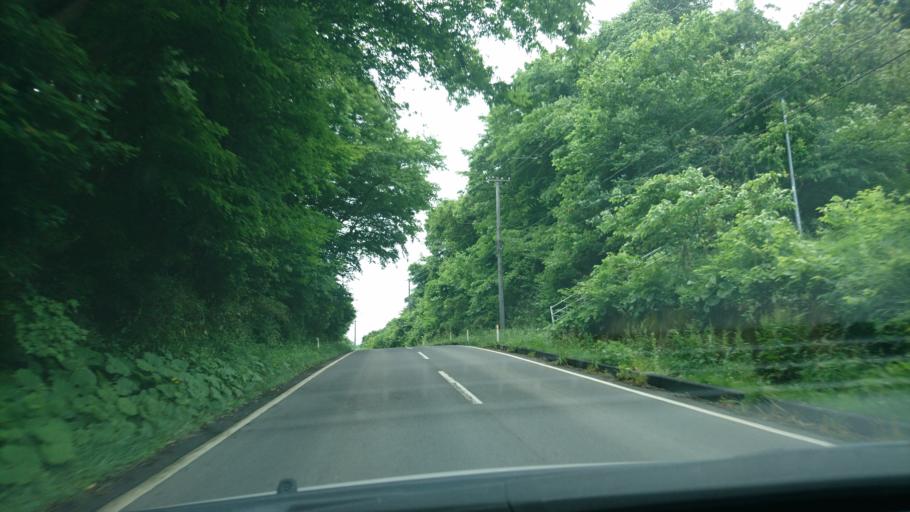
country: JP
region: Iwate
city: Ichinoseki
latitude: 38.9555
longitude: 141.0536
